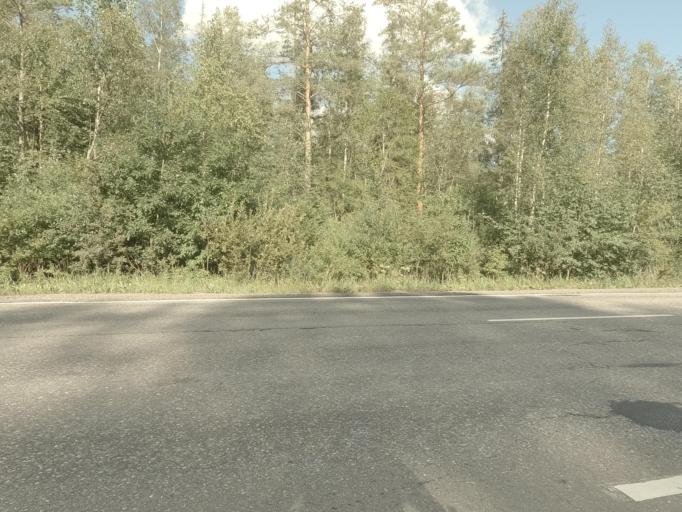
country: RU
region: Leningrad
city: Shcheglovo
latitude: 60.0008
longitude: 30.8704
